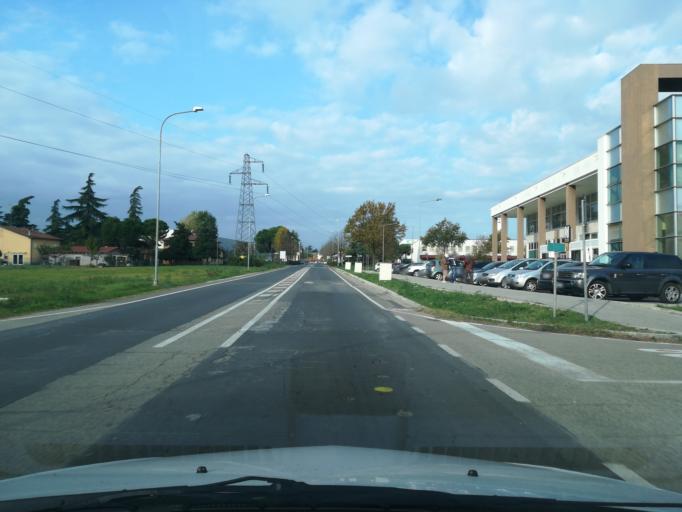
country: IT
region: Emilia-Romagna
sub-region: Provincia di Bologna
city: Imola
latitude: 44.3666
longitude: 11.7090
